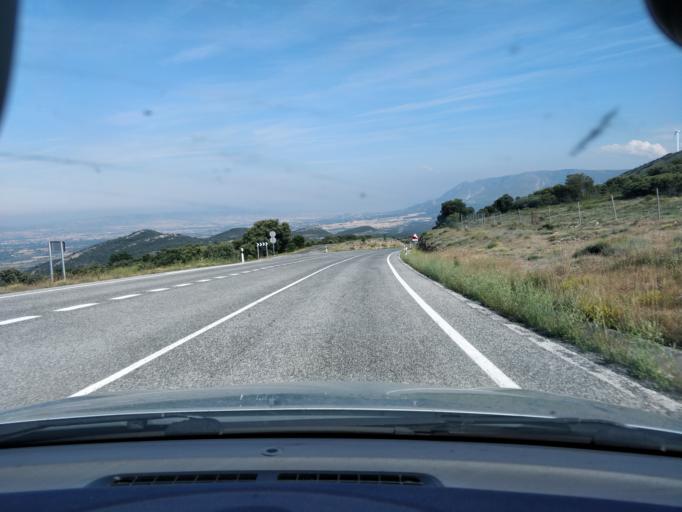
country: ES
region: Castille and Leon
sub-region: Provincia de Burgos
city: Medina de Pomar
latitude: 42.9251
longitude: -3.6316
